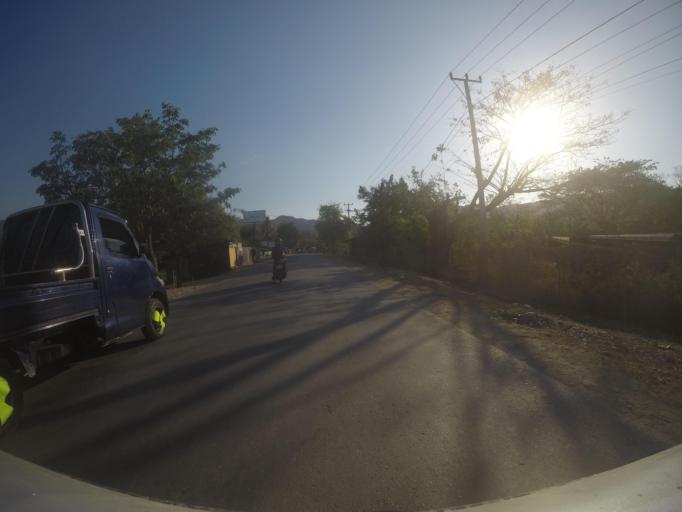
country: TL
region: Dili
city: Dili
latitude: -8.5527
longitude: 125.6598
